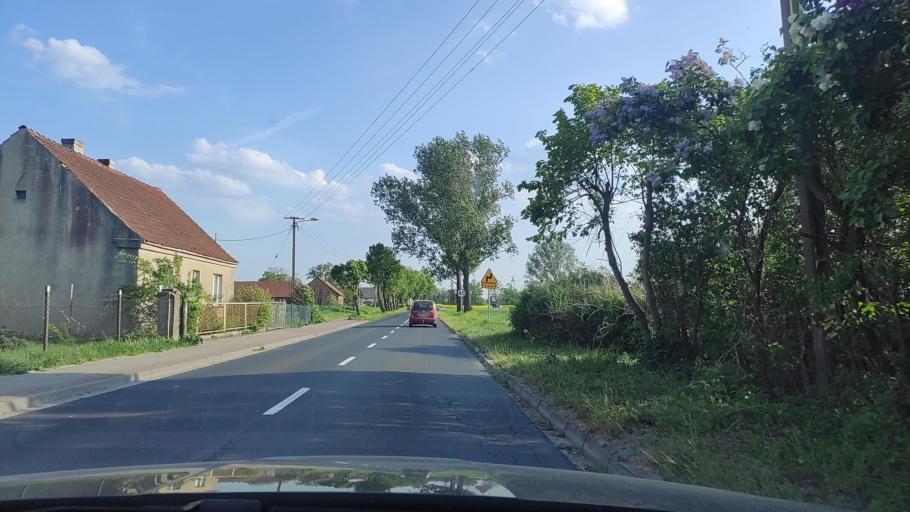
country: PL
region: Greater Poland Voivodeship
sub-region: Powiat poznanski
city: Kleszczewo
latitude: 52.3531
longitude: 17.1722
